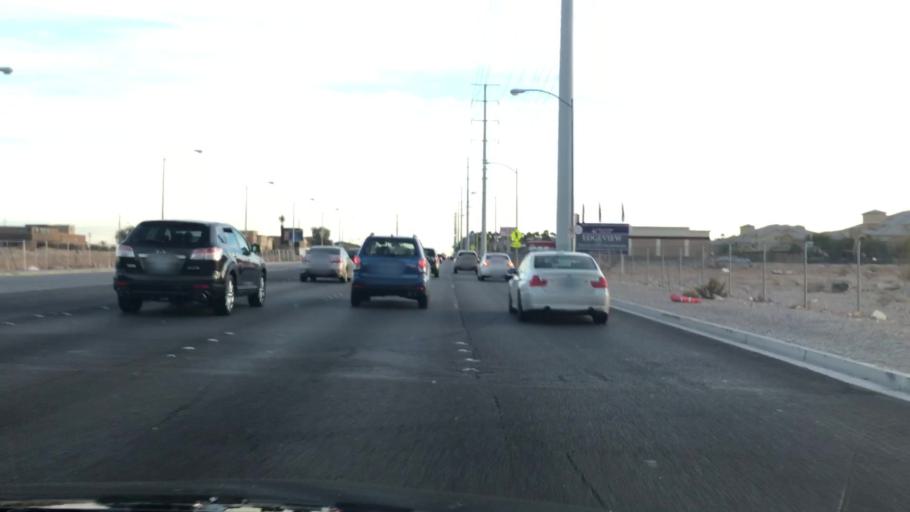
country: US
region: Nevada
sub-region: Clark County
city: Enterprise
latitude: 36.0631
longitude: -115.2795
